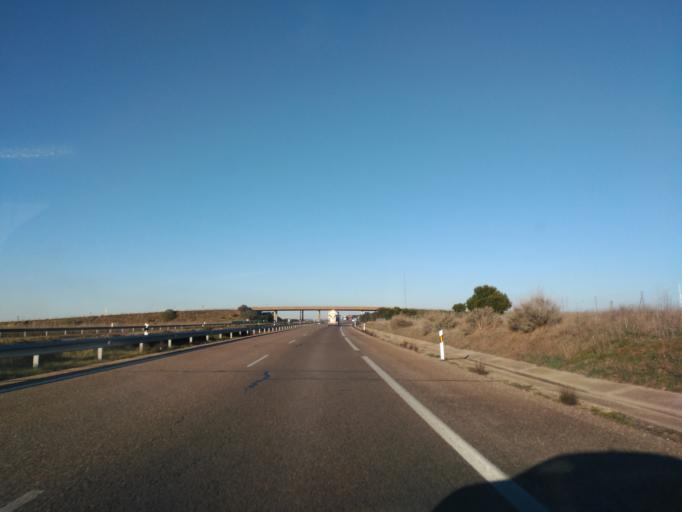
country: ES
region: Castille and Leon
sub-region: Provincia de Salamanca
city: Castellanos de Moriscos
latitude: 41.0267
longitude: -5.5756
